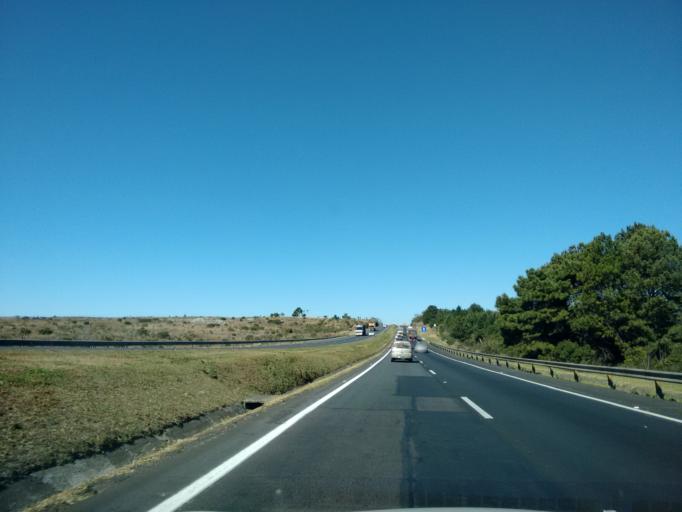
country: BR
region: Parana
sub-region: Palmeira
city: Palmeira
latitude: -25.3871
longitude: -49.8026
